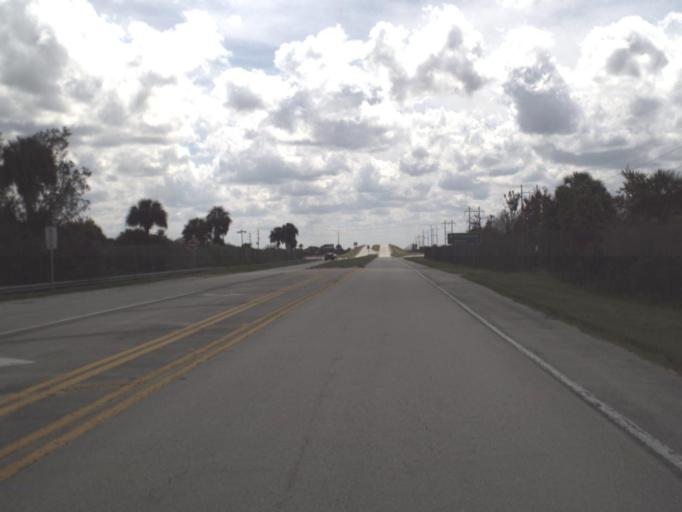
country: US
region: Florida
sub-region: Collier County
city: Immokalee
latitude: 26.1623
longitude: -81.3453
